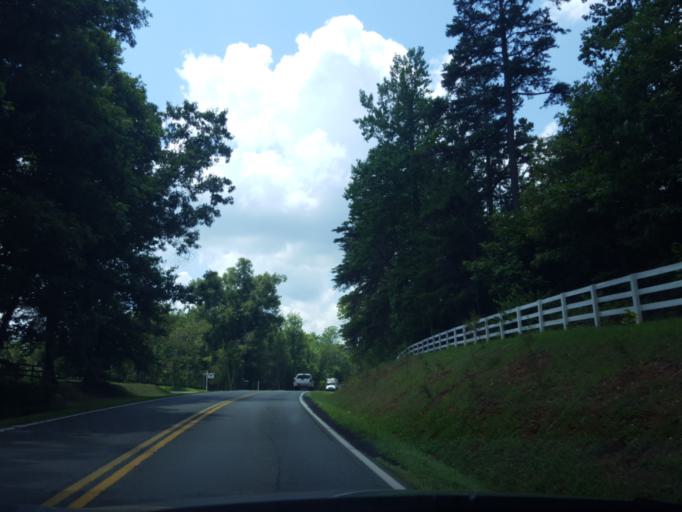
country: US
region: Virginia
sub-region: Orange County
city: Gordonsville
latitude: 38.0739
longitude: -78.2949
